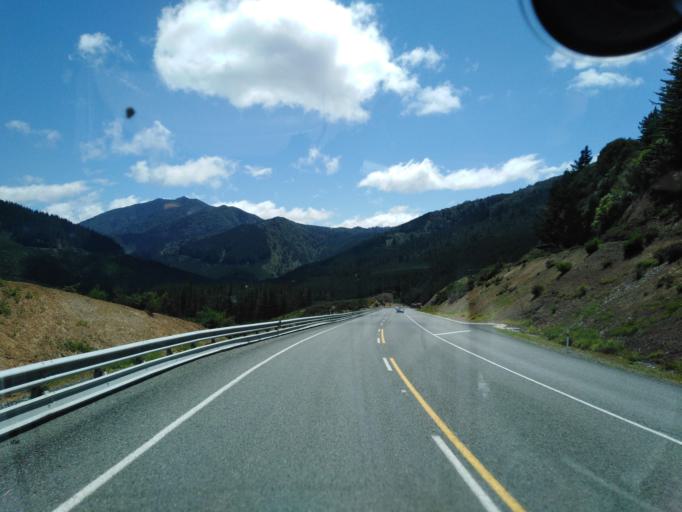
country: NZ
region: Nelson
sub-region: Nelson City
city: Nelson
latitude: -41.1877
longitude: 173.5543
